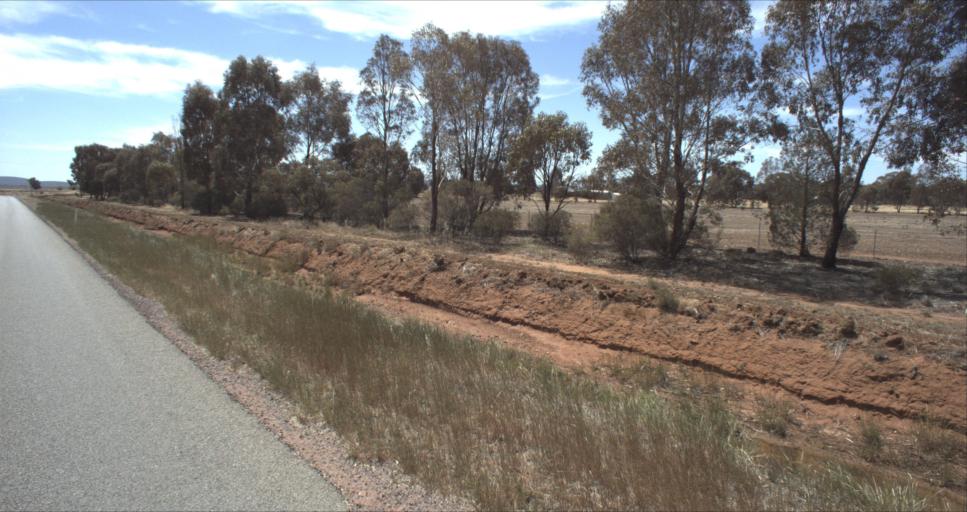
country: AU
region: New South Wales
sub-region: Leeton
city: Leeton
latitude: -34.5590
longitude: 146.4532
